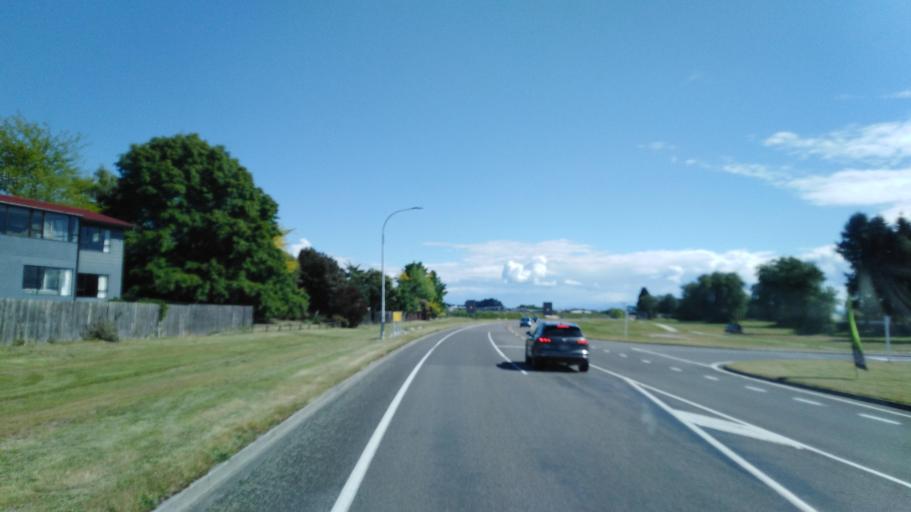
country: NZ
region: Waikato
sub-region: Taupo District
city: Taupo
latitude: -38.7189
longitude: 176.0817
